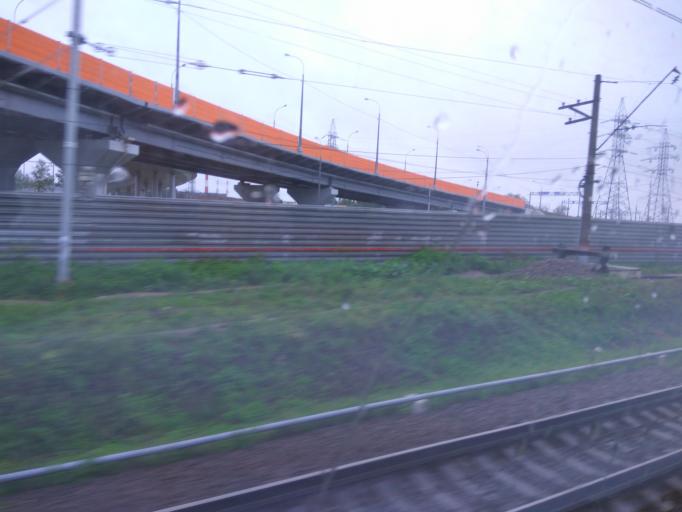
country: RU
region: Moskovskaya
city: Stupino
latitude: 54.9047
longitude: 38.0829
